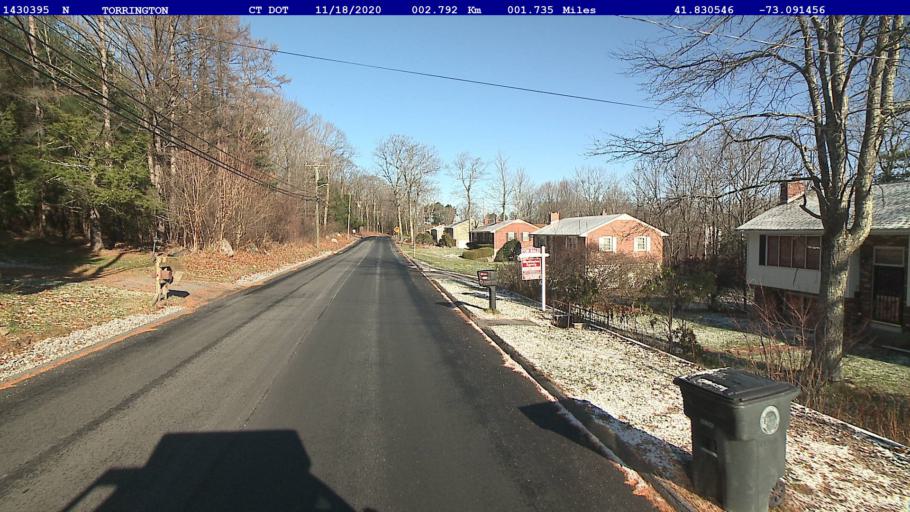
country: US
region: Connecticut
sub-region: Litchfield County
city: Torrington
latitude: 41.8306
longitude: -73.0914
